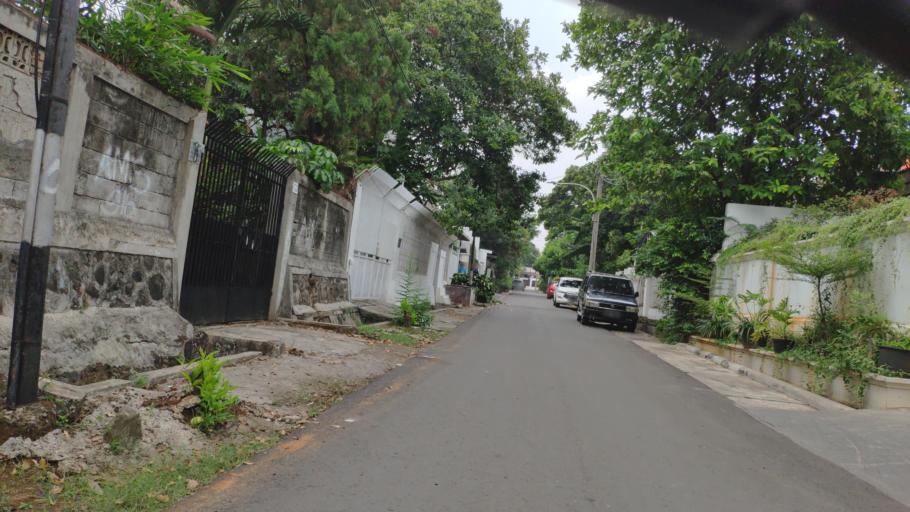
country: ID
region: Jakarta Raya
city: Jakarta
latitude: -6.2691
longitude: 106.7960
